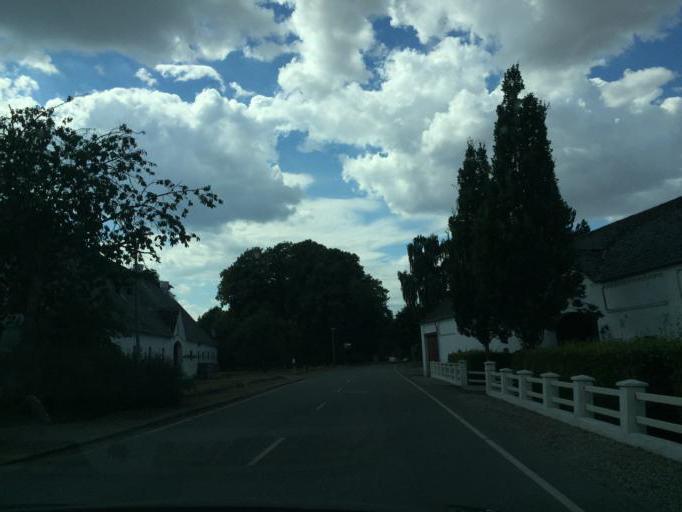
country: DK
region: South Denmark
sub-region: Assens Kommune
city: Harby
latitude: 55.2133
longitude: 10.0316
